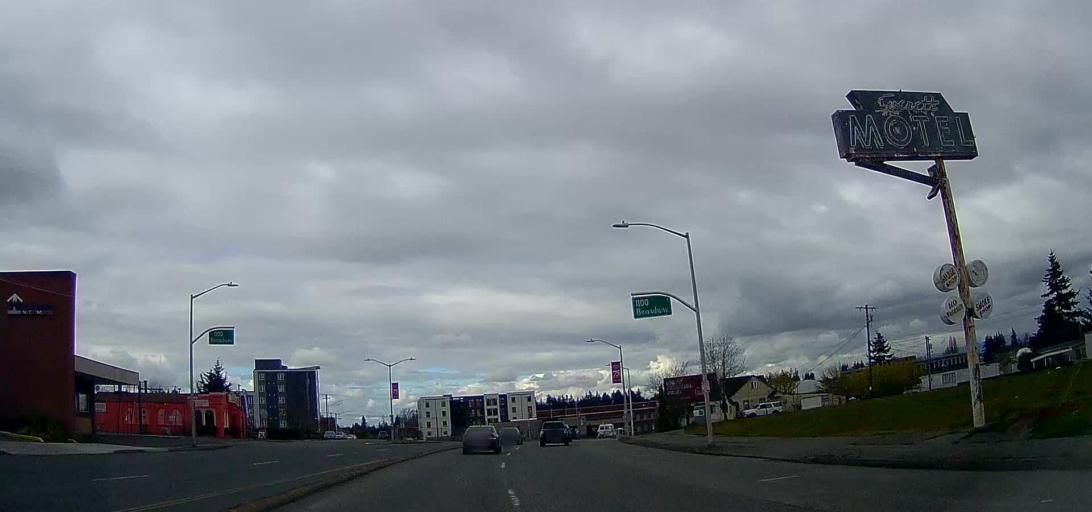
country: US
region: Washington
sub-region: Snohomish County
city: Everett
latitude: 48.0022
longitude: -122.2009
